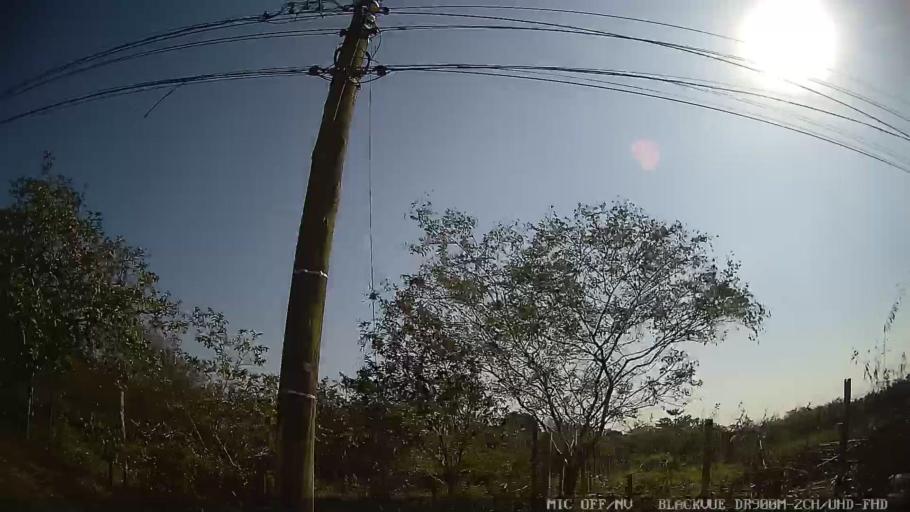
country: BR
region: Sao Paulo
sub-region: Guaruja
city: Guaruja
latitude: -24.0086
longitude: -46.2892
